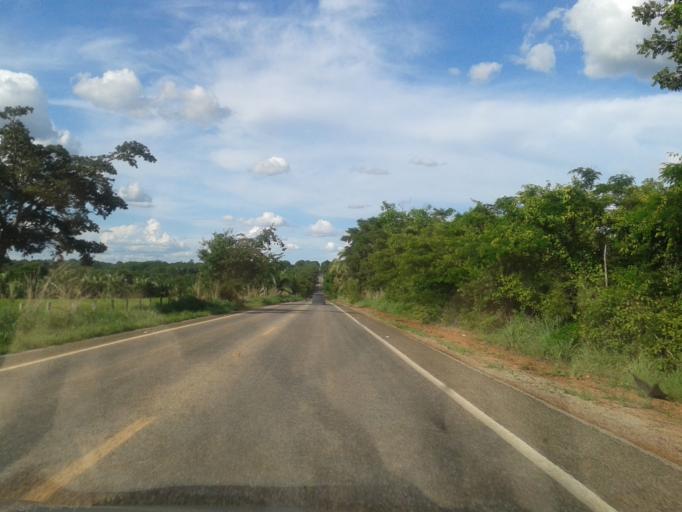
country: BR
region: Goias
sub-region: Mozarlandia
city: Mozarlandia
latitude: -14.4609
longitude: -50.4663
